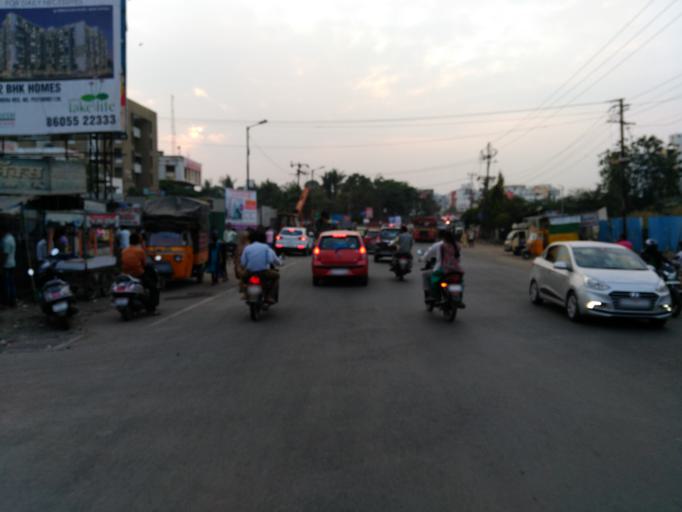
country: IN
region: Maharashtra
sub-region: Pune Division
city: Pune
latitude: 18.4497
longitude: 73.8741
